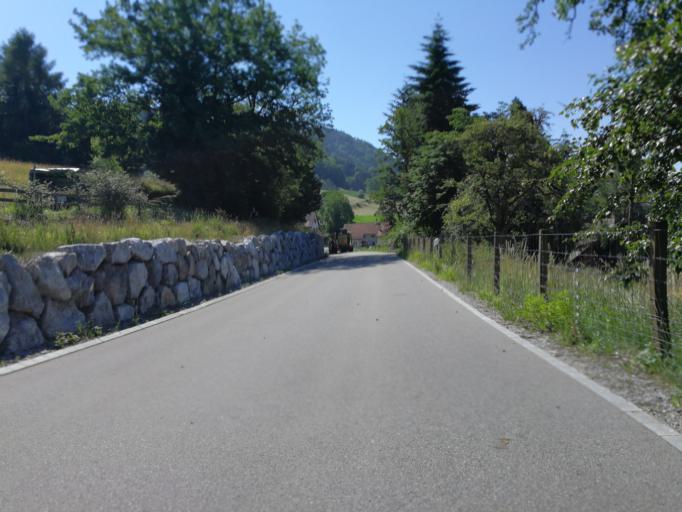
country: CH
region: Zurich
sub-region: Bezirk Hinwil
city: Hadlikon
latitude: 47.2960
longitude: 8.8685
